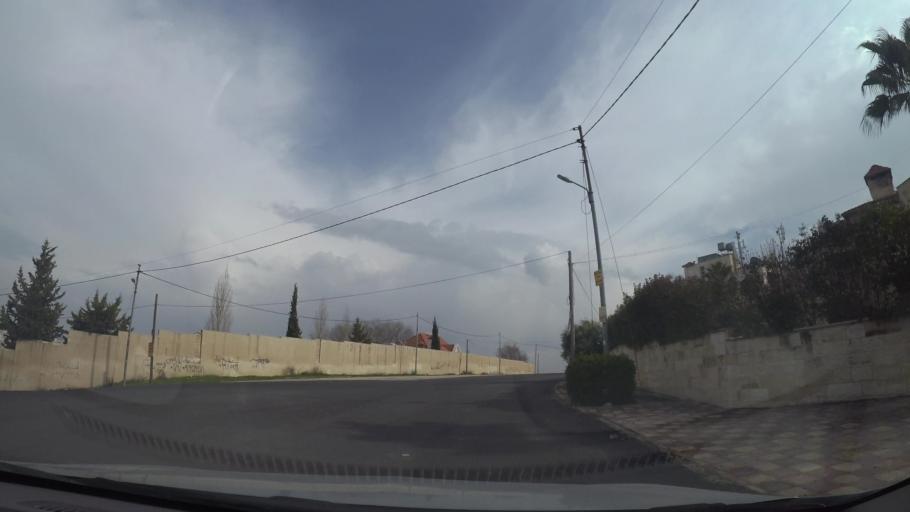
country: JO
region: Amman
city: Umm as Summaq
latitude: 31.8875
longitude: 35.8701
